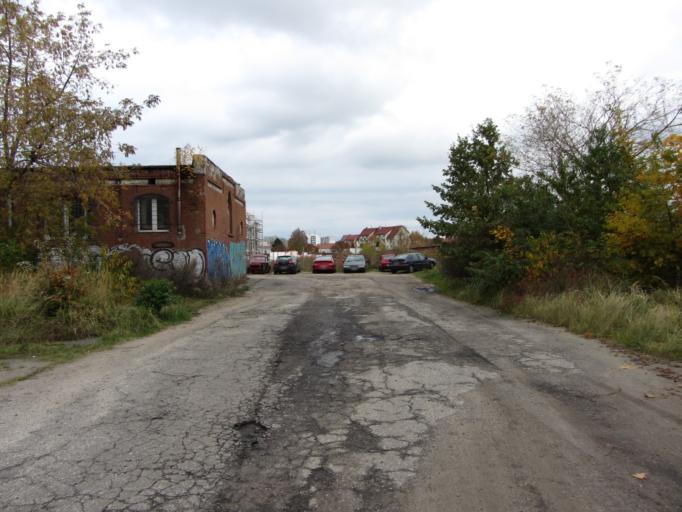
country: PL
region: West Pomeranian Voivodeship
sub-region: Powiat kolobrzeski
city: Kolobrzeg
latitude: 54.1676
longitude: 15.5635
